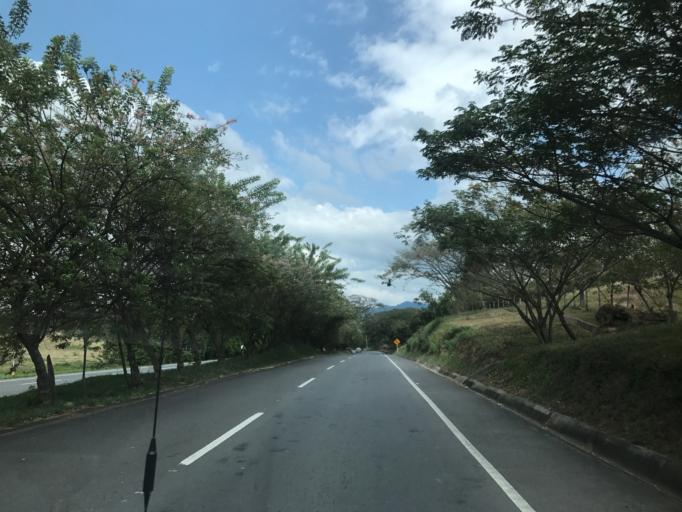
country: CO
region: Valle del Cauca
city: Obando
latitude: 4.6003
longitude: -75.9622
